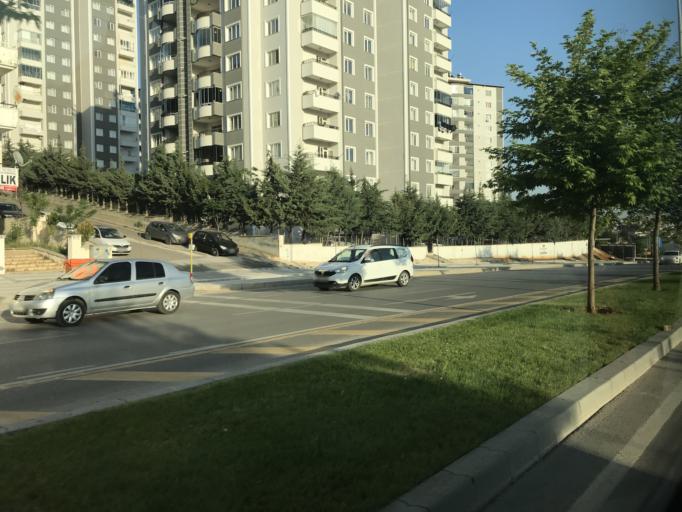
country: TR
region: Gaziantep
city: Sahinbey
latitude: 37.0686
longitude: 37.3195
